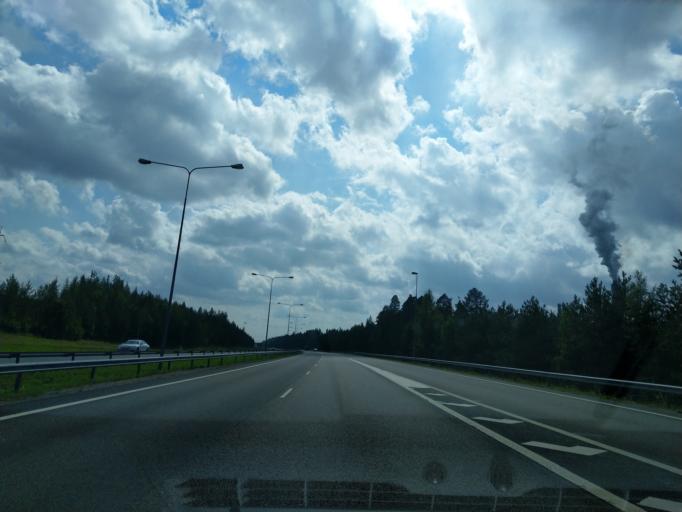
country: FI
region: South Karelia
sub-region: Imatra
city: Ruokolahti
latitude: 61.2534
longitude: 28.8798
